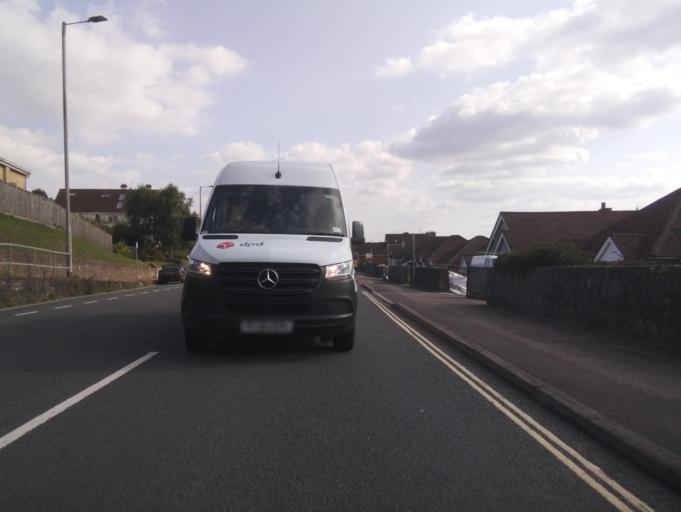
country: GB
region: England
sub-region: Devon
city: Exeter
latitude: 50.7453
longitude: -3.5476
